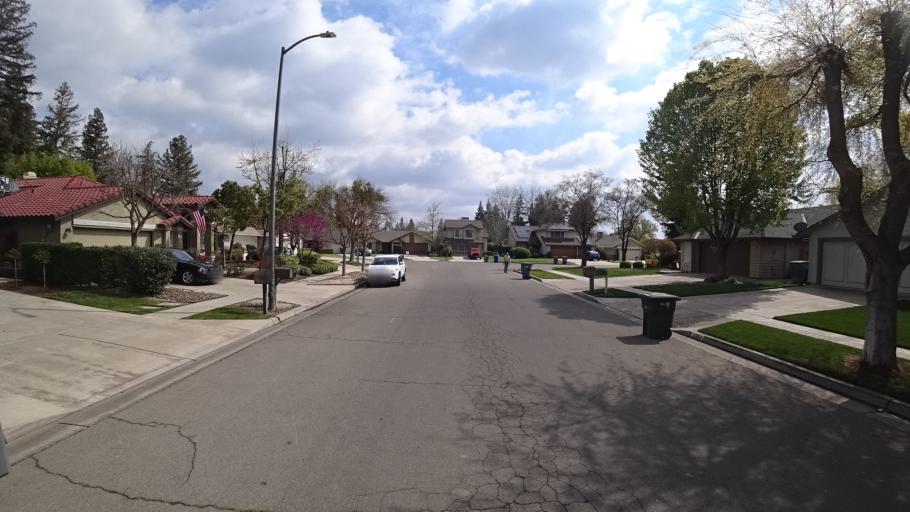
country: US
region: California
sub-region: Fresno County
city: Fresno
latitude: 36.8408
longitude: -119.8541
